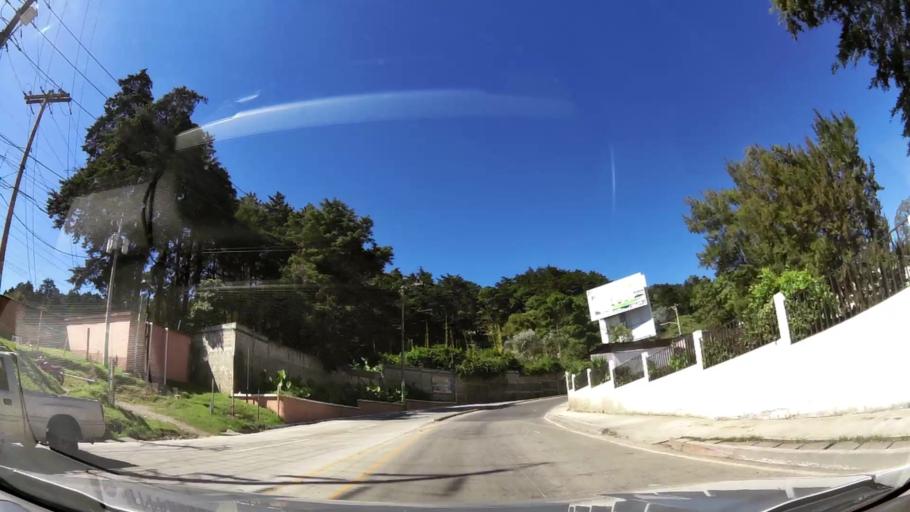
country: GT
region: Guatemala
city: San Jose Pinula
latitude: 14.5466
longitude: -90.4176
